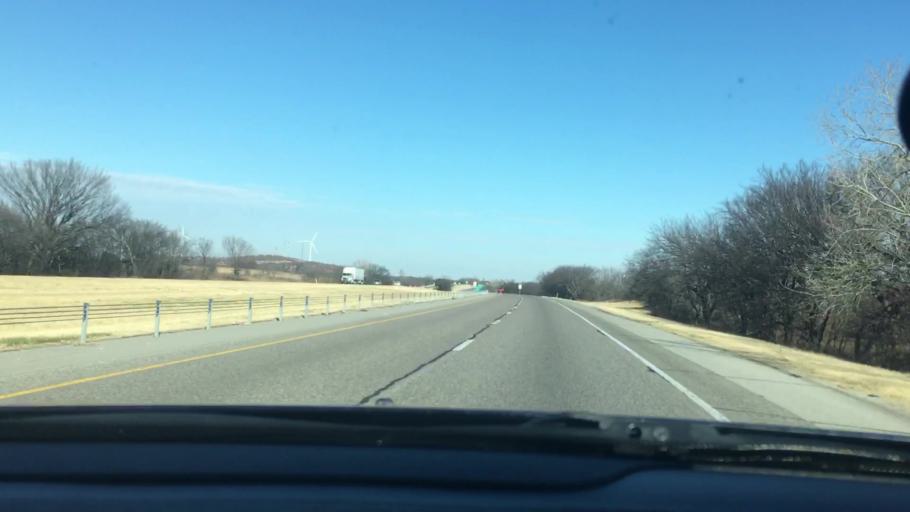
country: US
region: Oklahoma
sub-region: Murray County
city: Davis
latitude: 34.3858
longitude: -97.1417
